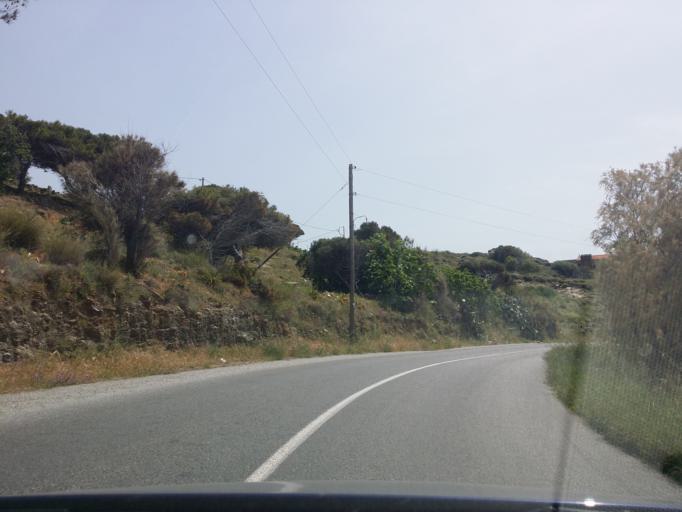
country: GR
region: South Aegean
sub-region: Nomos Kykladon
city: Kea
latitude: 37.6616
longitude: 24.3186
